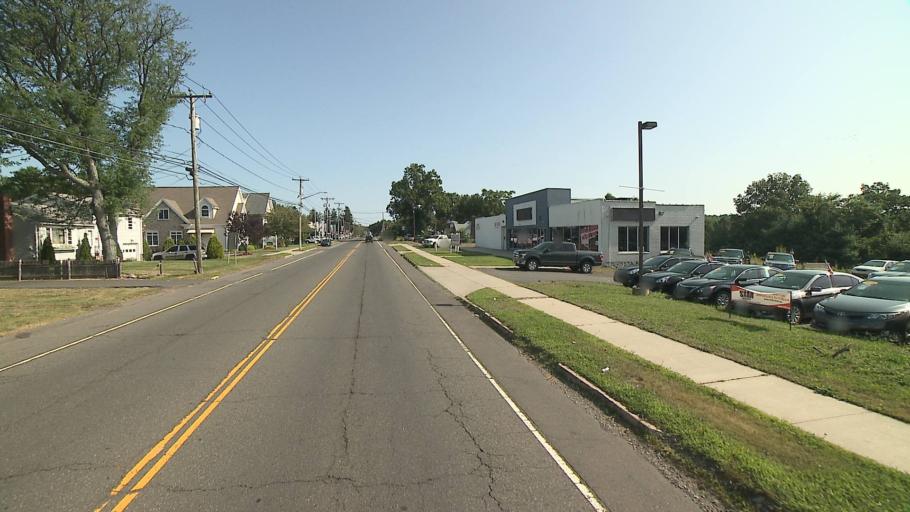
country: US
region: Connecticut
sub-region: New Haven County
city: Meriden
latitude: 41.5171
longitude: -72.8040
